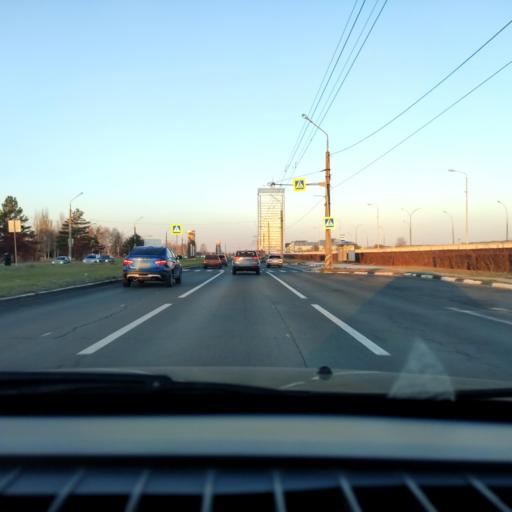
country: RU
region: Samara
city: Tol'yatti
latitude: 53.5546
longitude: 49.2764
